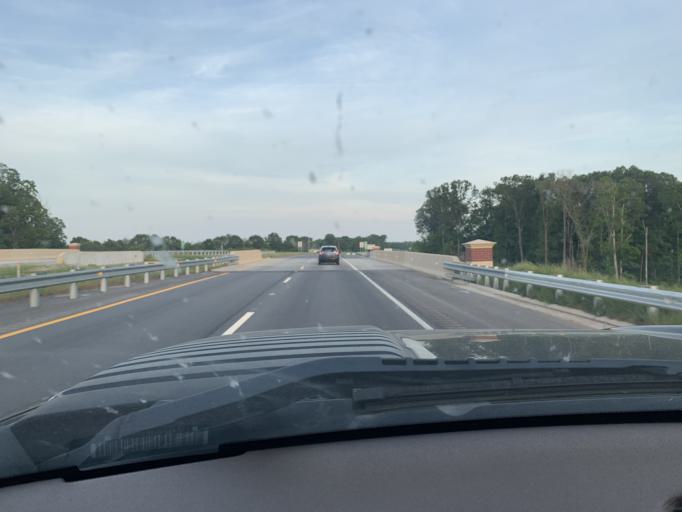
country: US
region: North Carolina
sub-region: Union County
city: Lake Park
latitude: 35.0579
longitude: -80.5833
